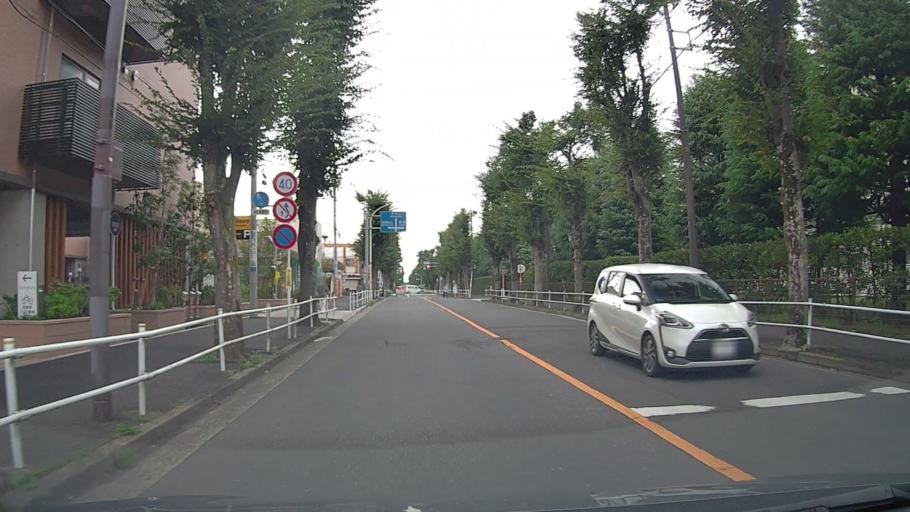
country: JP
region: Tokyo
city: Tanashicho
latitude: 35.7454
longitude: 139.5053
